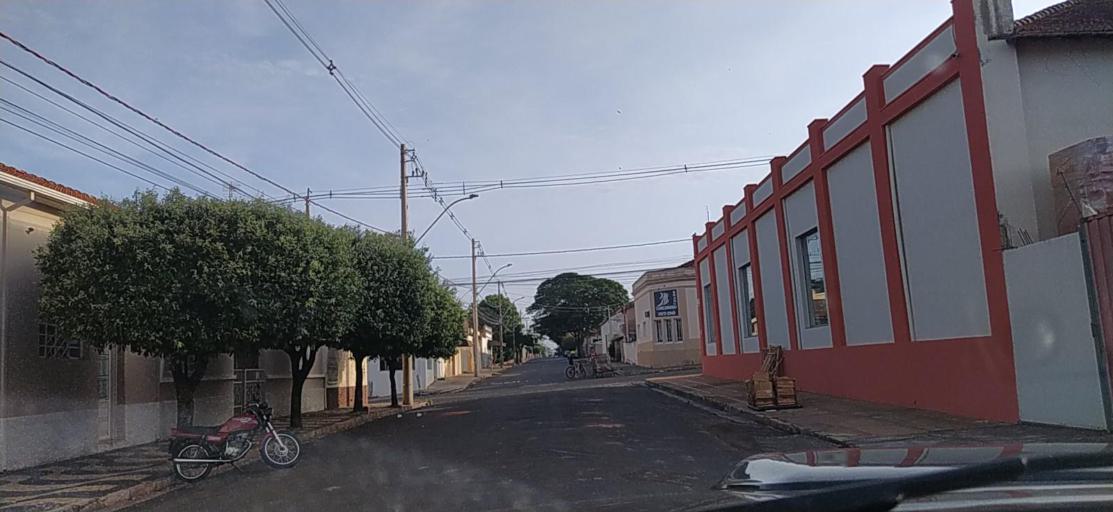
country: BR
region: Sao Paulo
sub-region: Pindorama
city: Pindorama
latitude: -21.1897
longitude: -48.9033
